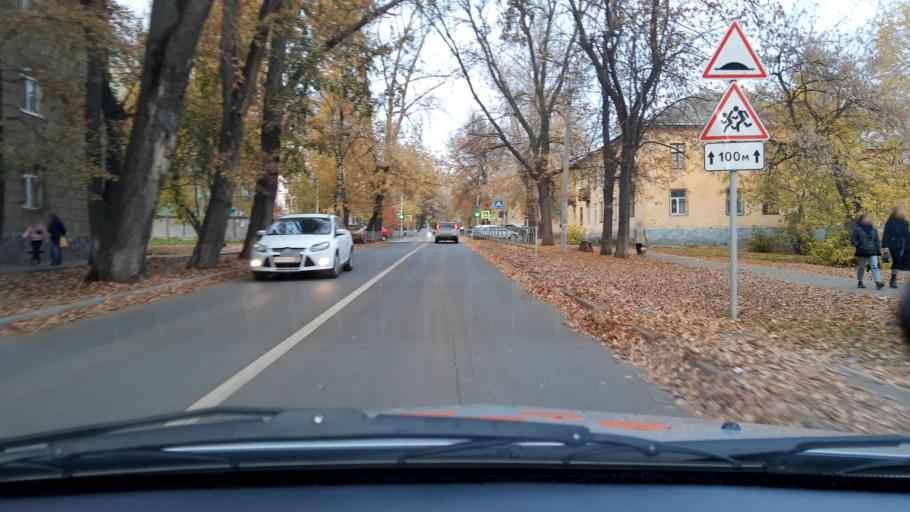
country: RU
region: Bashkortostan
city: Ufa
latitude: 54.8134
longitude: 56.0966
